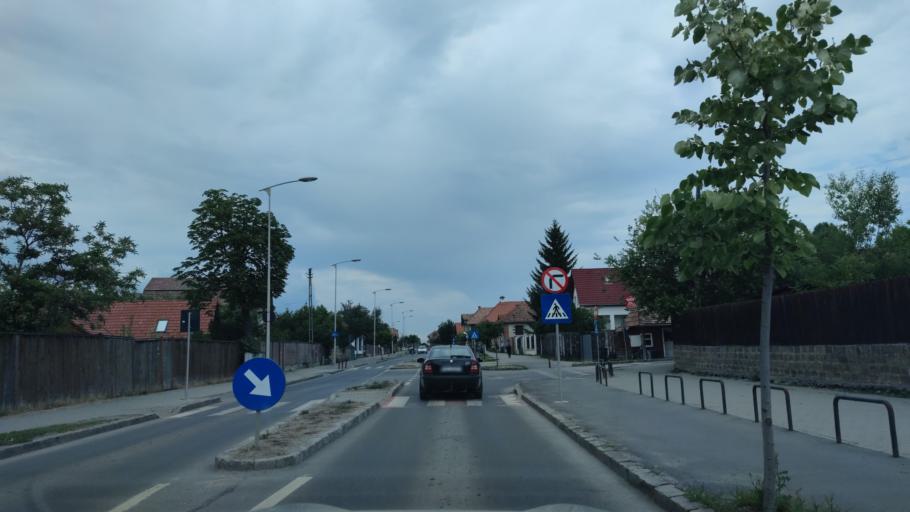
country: RO
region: Harghita
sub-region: Municipiul Miercurea Ciuc
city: Miercurea-Ciuc
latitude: 46.3699
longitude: 25.8053
